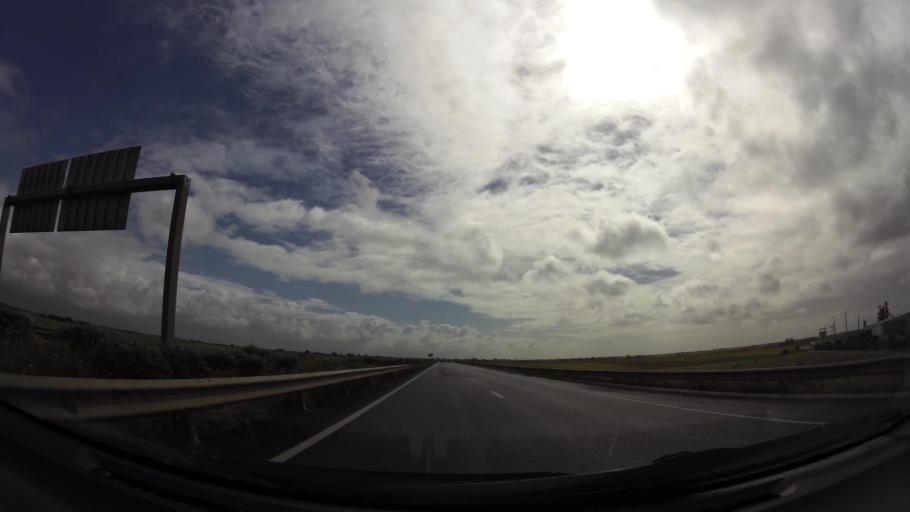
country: MA
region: Grand Casablanca
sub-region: Nouaceur
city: Dar Bouazza
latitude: 33.3453
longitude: -8.0054
